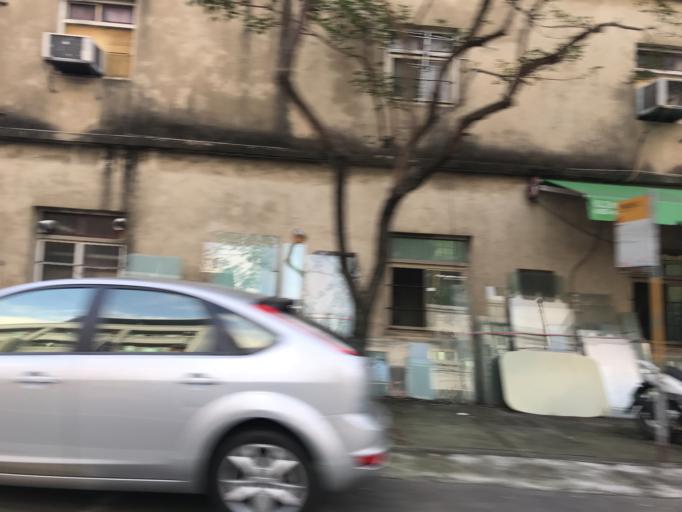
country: TW
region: Taiwan
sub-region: Taichung City
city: Taichung
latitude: 24.1159
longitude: 120.6923
